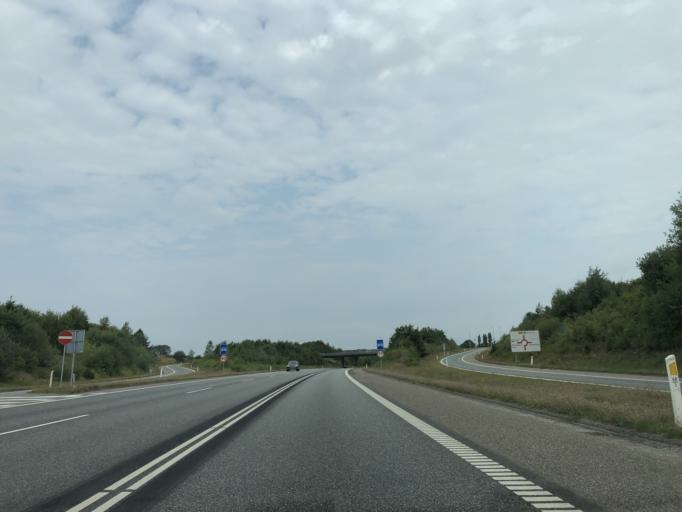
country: DK
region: Central Jutland
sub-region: Silkeborg Kommune
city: Kjellerup
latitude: 56.3381
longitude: 9.5370
